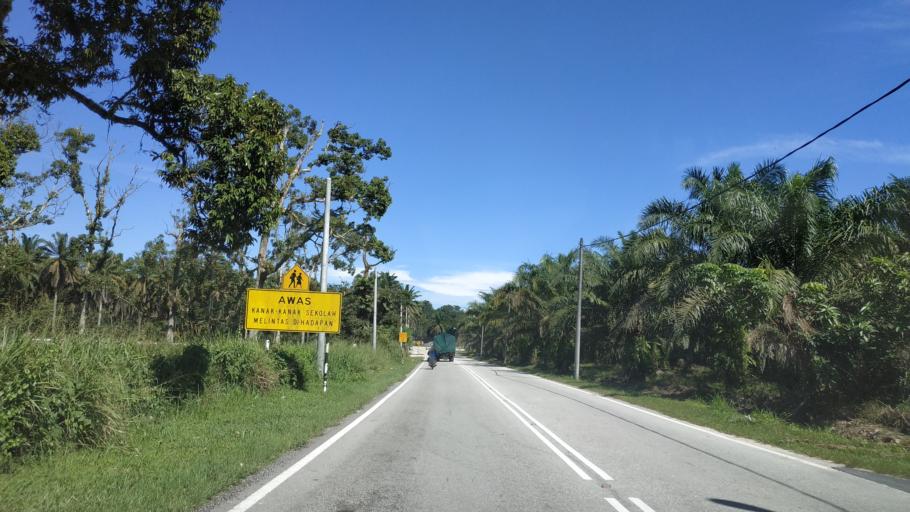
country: MY
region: Kedah
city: Kulim
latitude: 5.3156
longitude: 100.5401
